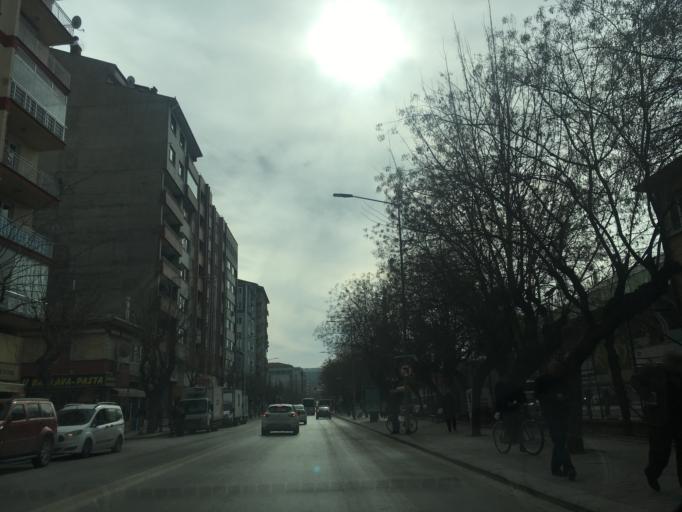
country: TR
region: Eskisehir
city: Eskisehir
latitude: 39.7722
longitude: 30.5143
